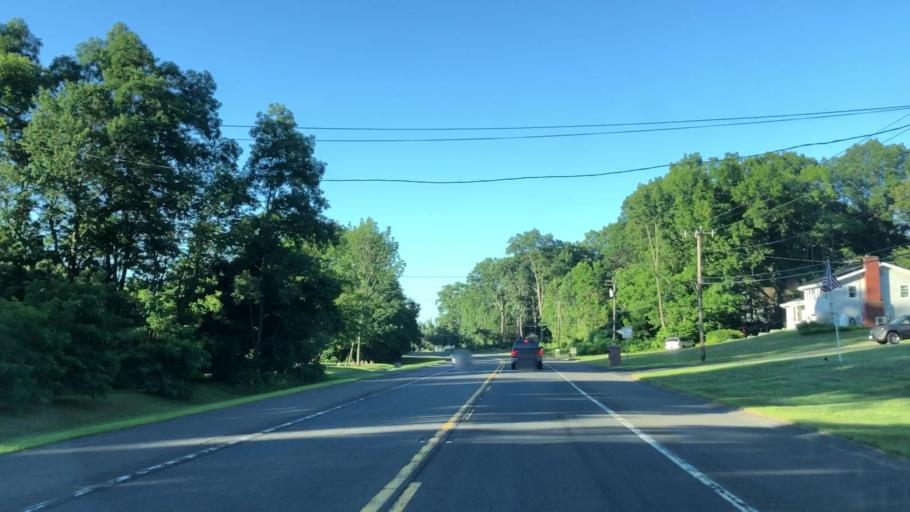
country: US
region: Massachusetts
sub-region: Hampshire County
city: Southampton
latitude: 42.2004
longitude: -72.7265
